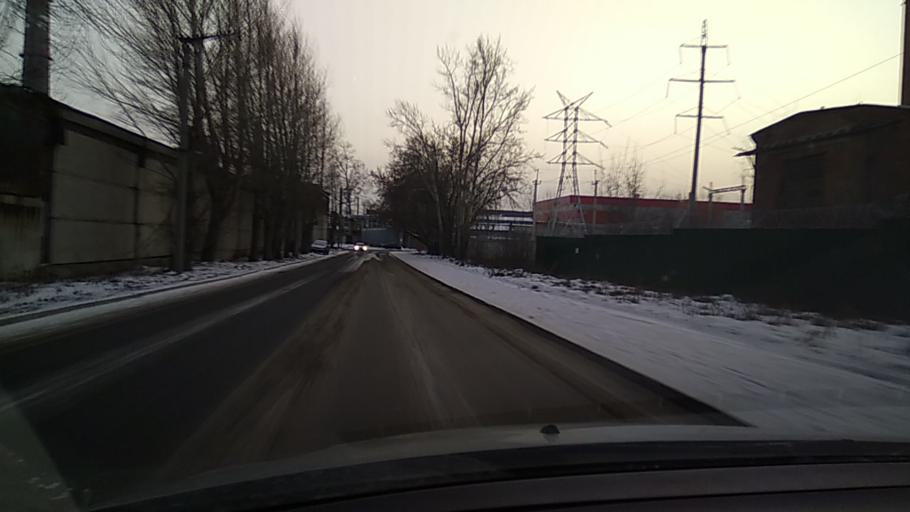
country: RU
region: Sverdlovsk
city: Istok
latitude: 56.7599
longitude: 60.7165
